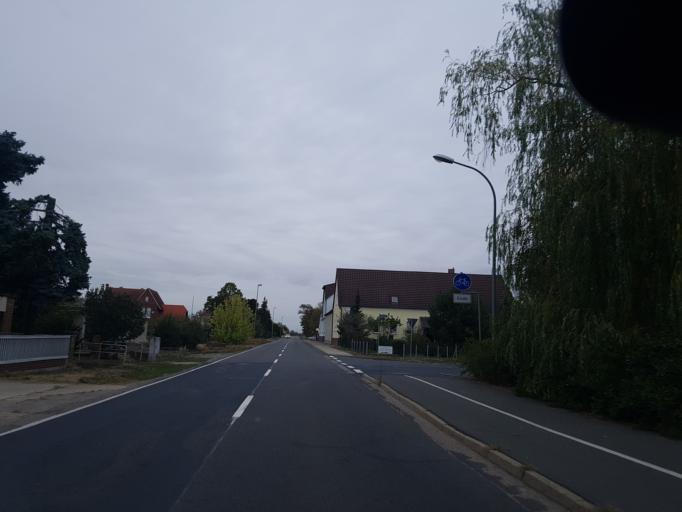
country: DE
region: Saxony-Anhalt
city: Prettin
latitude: 51.6670
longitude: 12.9179
